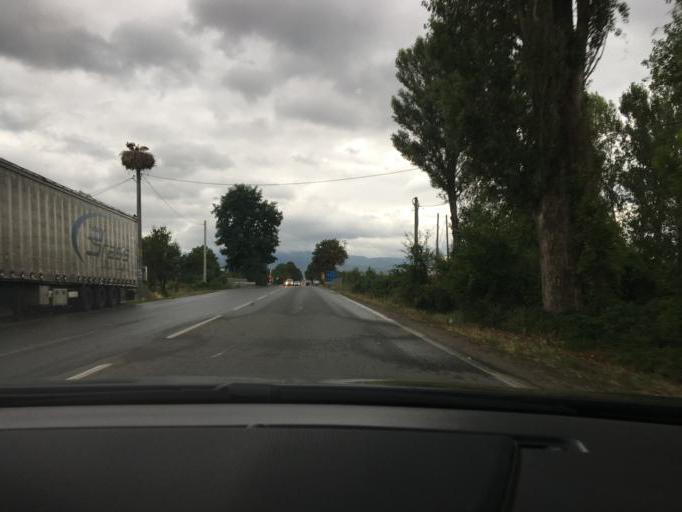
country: BG
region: Kyustendil
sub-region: Obshtina Kyustendil
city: Kyustendil
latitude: 42.2809
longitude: 22.7257
